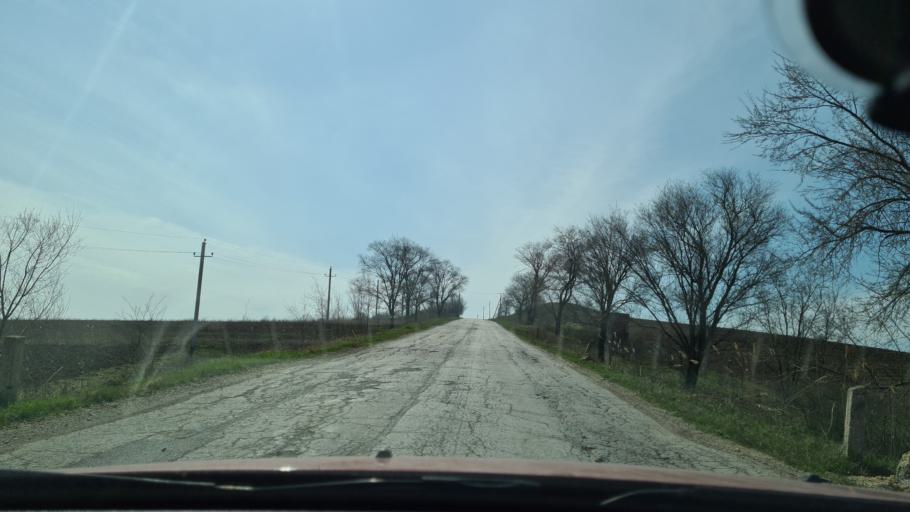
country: MD
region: Ungheni
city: Ungheni
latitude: 47.2925
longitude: 27.9175
